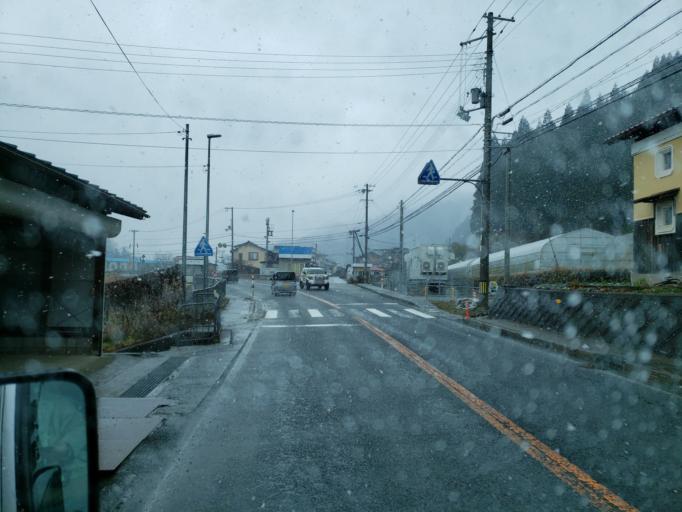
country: JP
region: Hyogo
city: Toyooka
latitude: 35.3859
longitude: 134.6795
